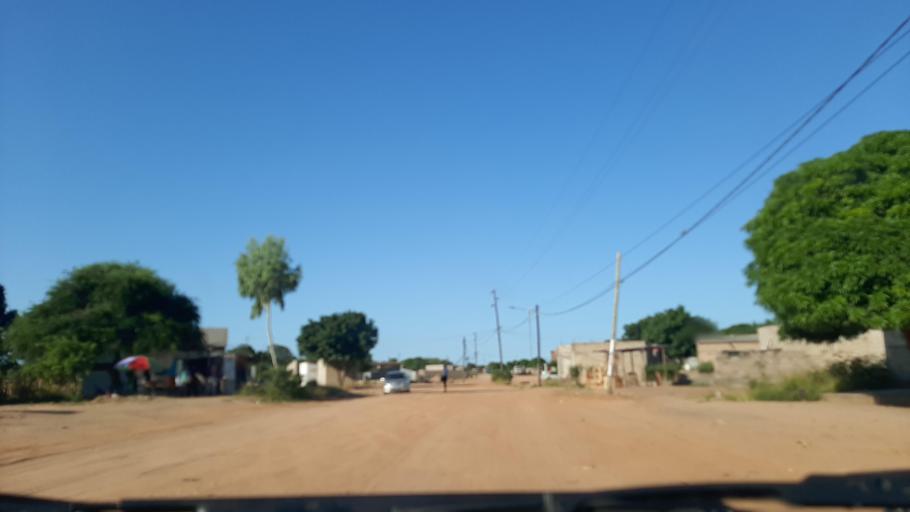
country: MZ
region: Maputo City
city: Maputo
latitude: -25.8008
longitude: 32.5494
